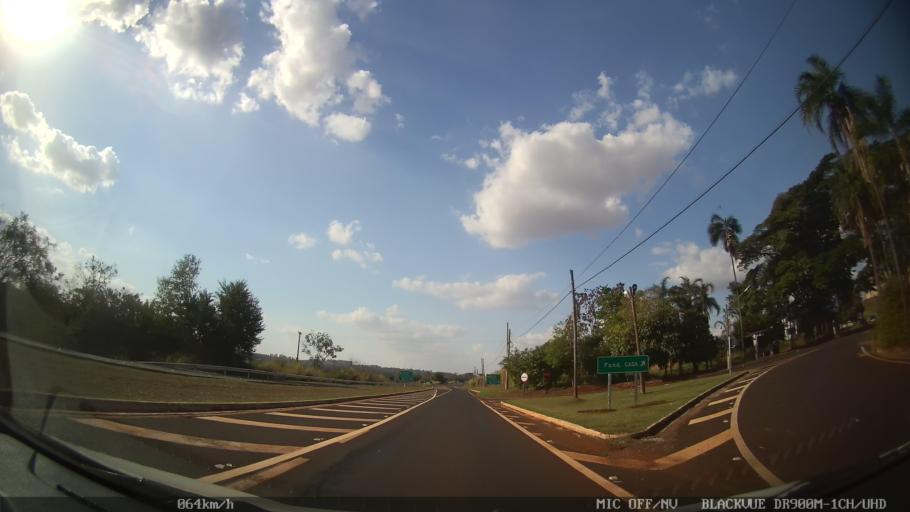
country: BR
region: Sao Paulo
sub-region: Ribeirao Preto
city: Ribeirao Preto
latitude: -21.1888
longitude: -47.8647
